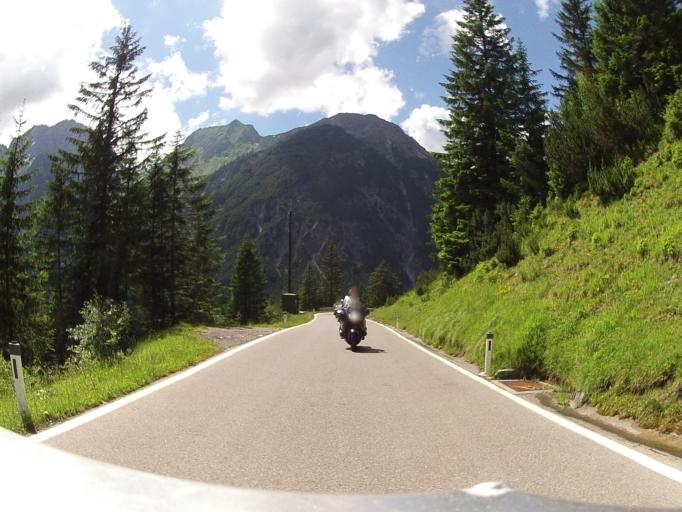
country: AT
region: Tyrol
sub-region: Politischer Bezirk Reutte
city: Gramais
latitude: 47.2845
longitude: 10.6134
